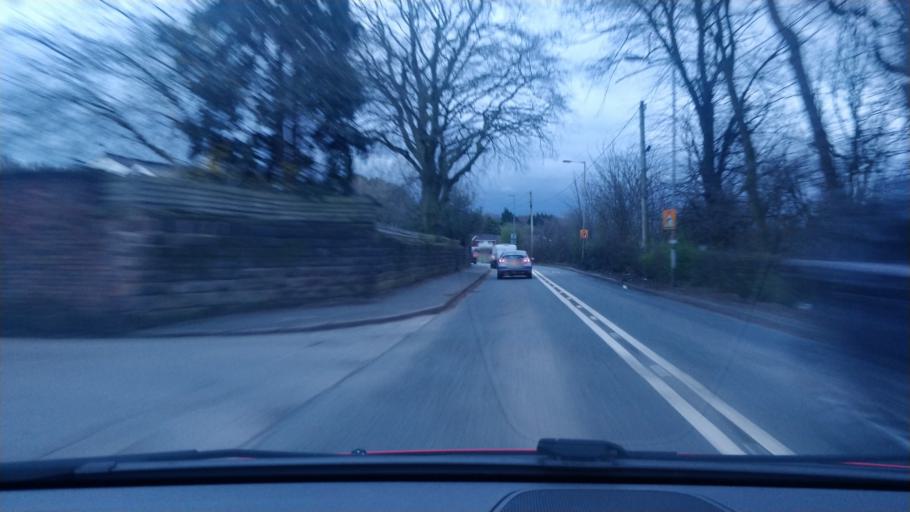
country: GB
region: England
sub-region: Knowsley
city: Knowsley
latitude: 53.4397
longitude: -2.8924
